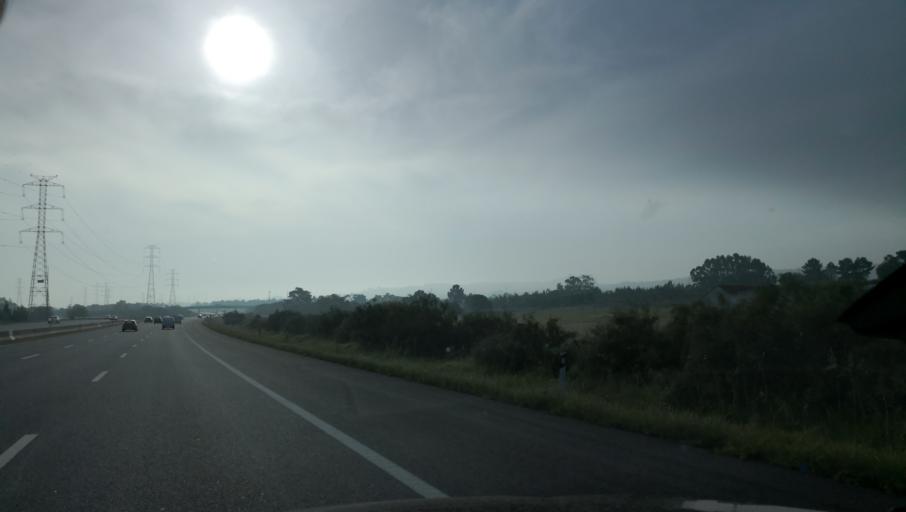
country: PT
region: Setubal
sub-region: Palmela
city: Quinta do Anjo
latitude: 38.5839
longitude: -8.9501
